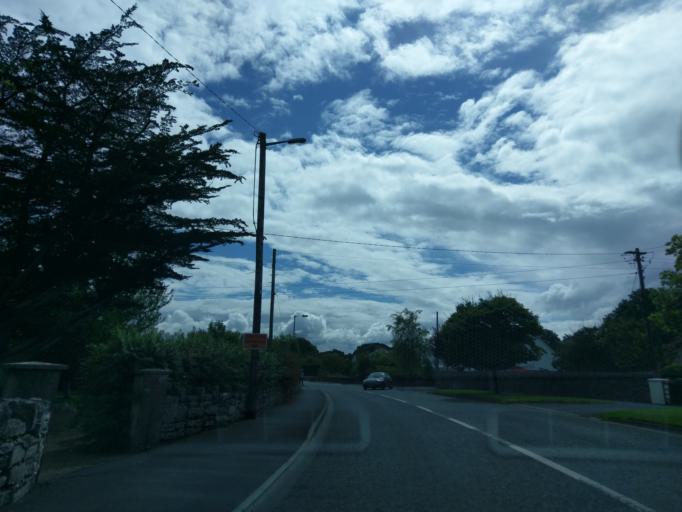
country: IE
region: Connaught
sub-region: County Galway
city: Oranmore
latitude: 53.2623
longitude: -8.9326
